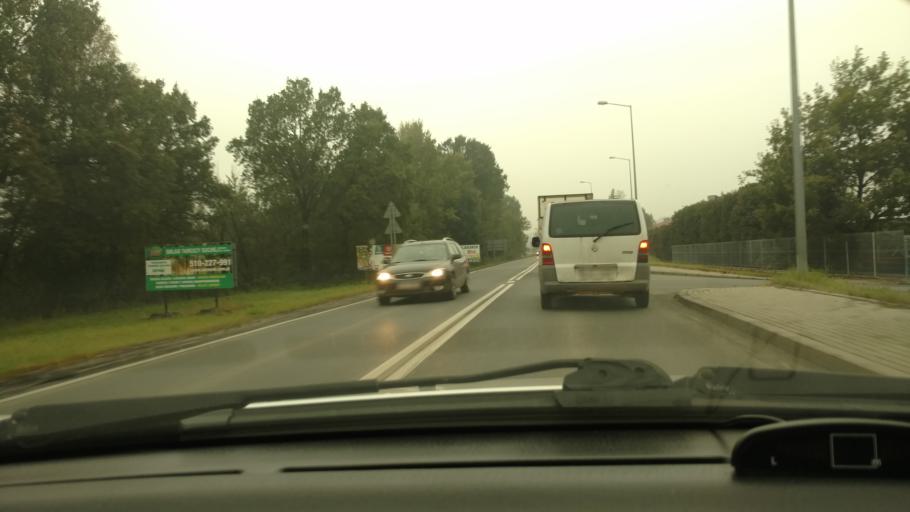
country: PL
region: Lesser Poland Voivodeship
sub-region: Powiat gorlicki
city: Kobylanka
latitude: 49.6887
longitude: 21.1953
